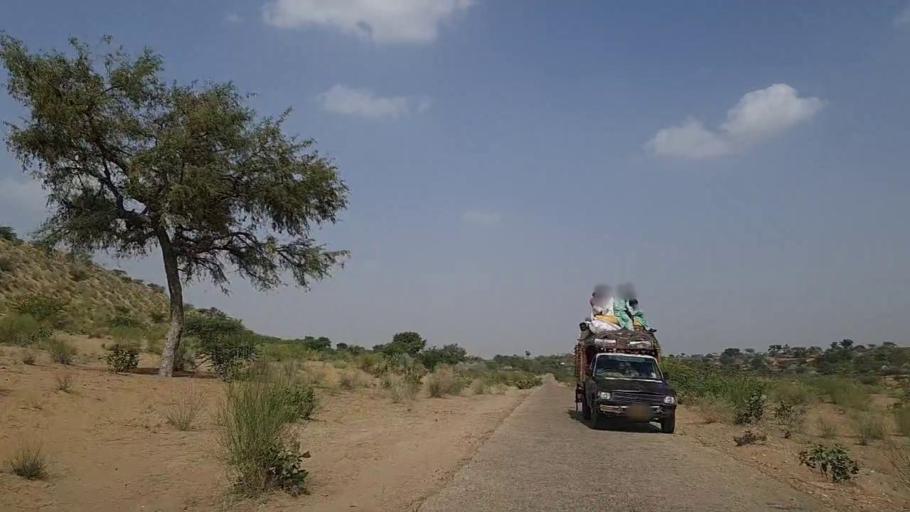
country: PK
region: Sindh
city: Islamkot
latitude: 24.7939
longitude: 70.1134
